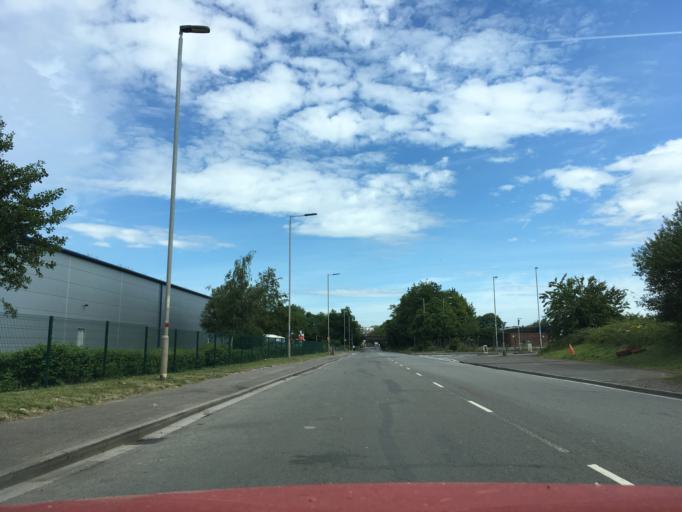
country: GB
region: Wales
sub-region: Newport
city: Nash
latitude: 51.5715
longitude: -2.9694
